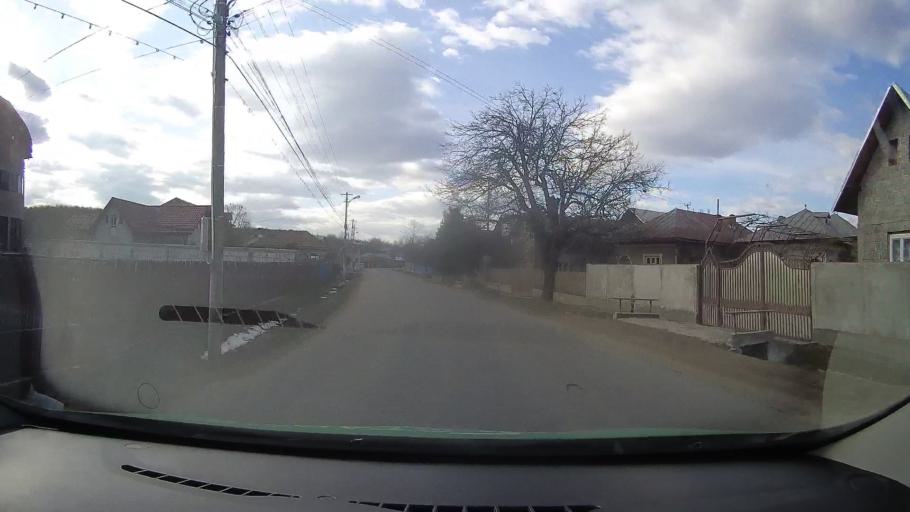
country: RO
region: Dambovita
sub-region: Comuna Ulmi
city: Ulmi
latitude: 44.8832
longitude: 25.5129
